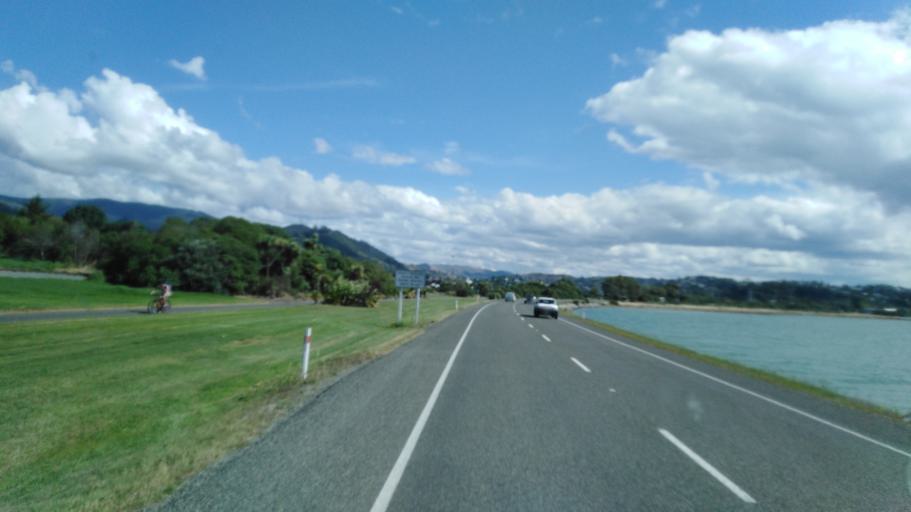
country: NZ
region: Nelson
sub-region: Nelson City
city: Nelson
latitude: -41.2601
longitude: 173.2946
